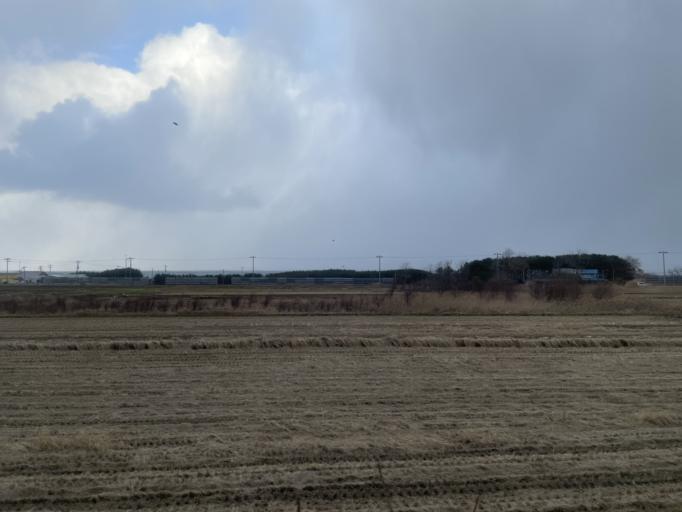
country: JP
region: Aomori
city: Mutsu
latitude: 41.1237
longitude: 141.2641
